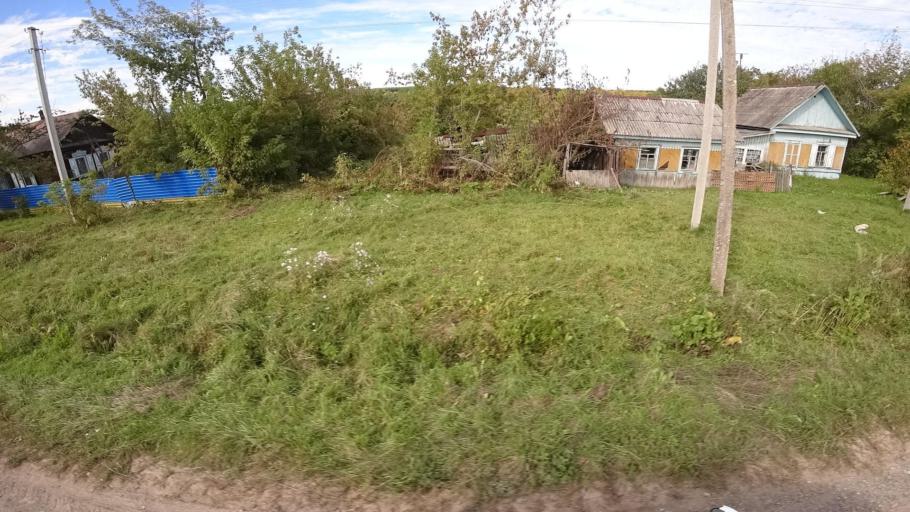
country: RU
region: Primorskiy
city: Dostoyevka
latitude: 44.3282
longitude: 133.4866
